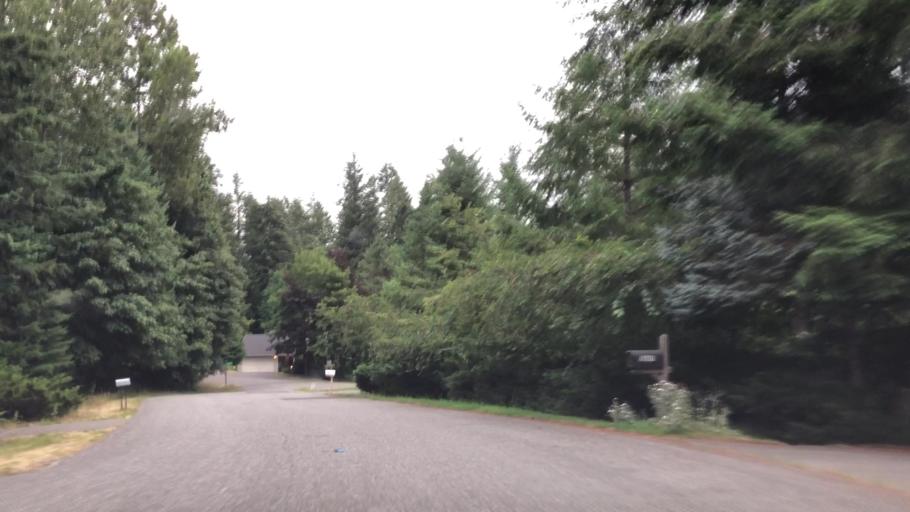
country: US
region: Washington
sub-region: King County
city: Cottage Lake
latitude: 47.7187
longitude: -122.0913
